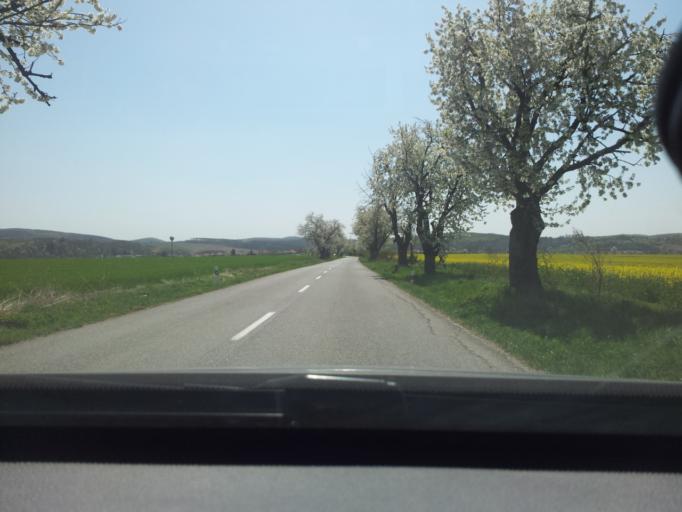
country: SK
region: Nitriansky
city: Zlate Moravce
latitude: 48.3189
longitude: 18.4409
